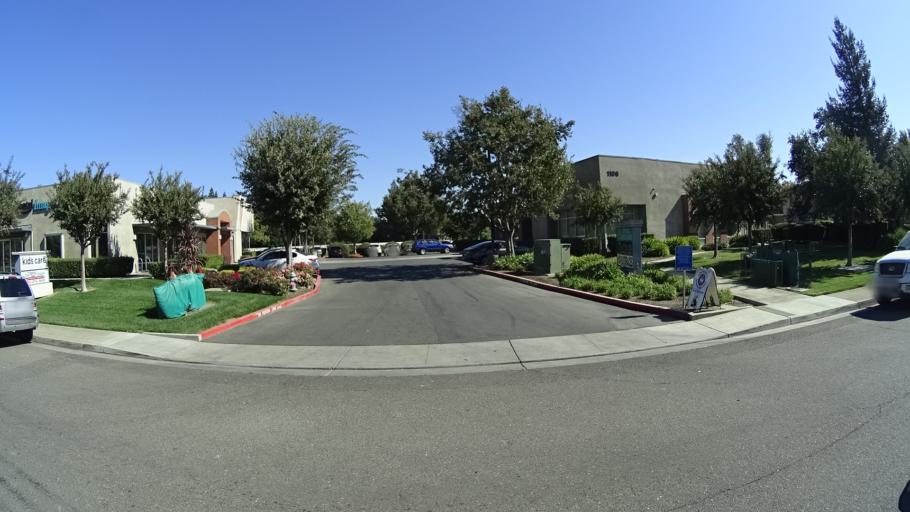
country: US
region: California
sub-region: Sacramento County
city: Parkway
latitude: 38.4911
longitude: -121.5161
